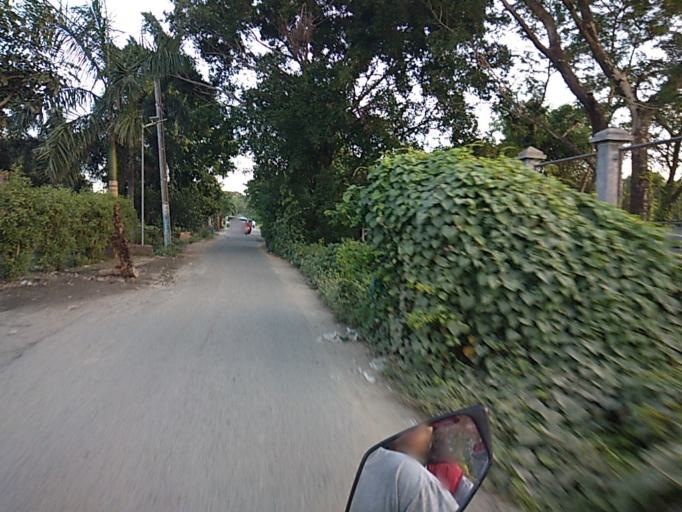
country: PH
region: Central Luzon
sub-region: Province of Bulacan
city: Paombong
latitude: 14.8613
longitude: 120.7657
